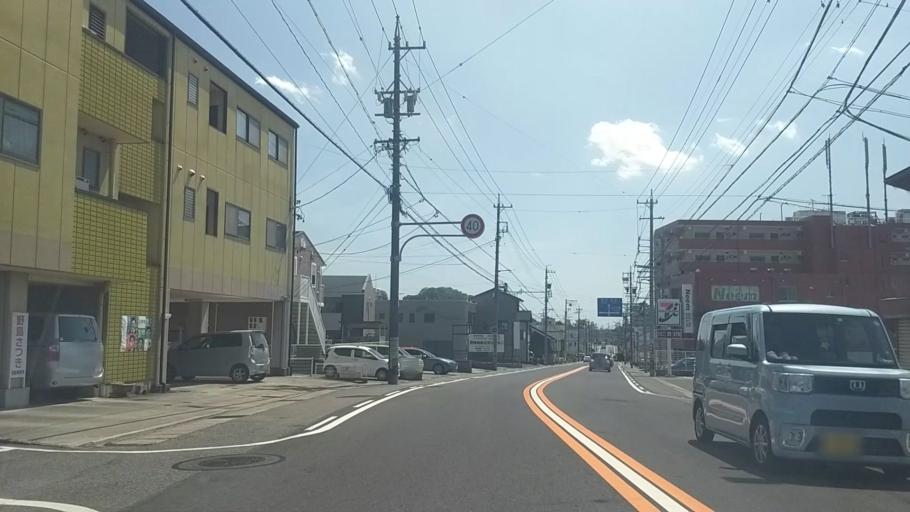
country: JP
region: Aichi
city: Okazaki
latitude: 34.9739
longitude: 137.1684
